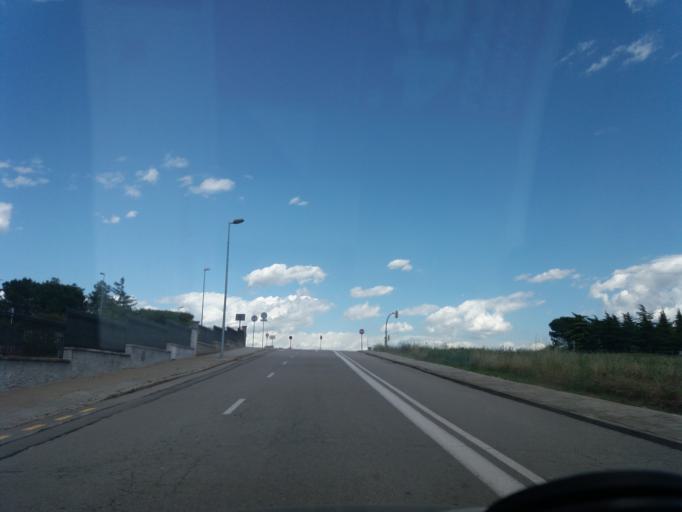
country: ES
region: Catalonia
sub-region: Provincia de Barcelona
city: Sant Fruitos de Bages
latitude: 41.7551
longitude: 1.8397
